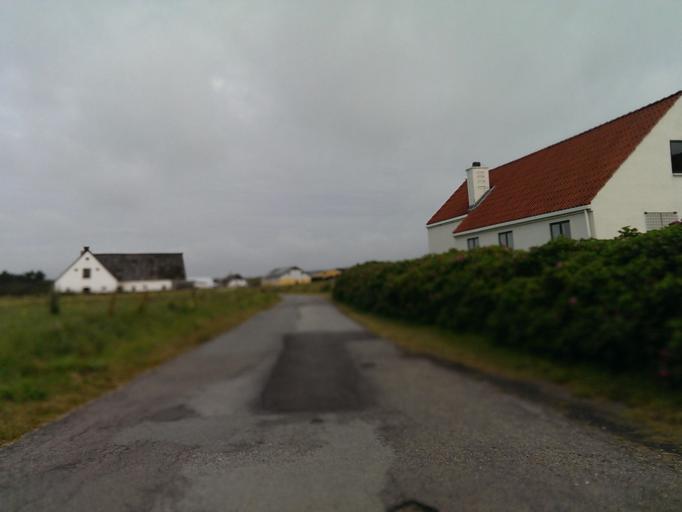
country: DK
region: North Denmark
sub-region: Jammerbugt Kommune
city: Pandrup
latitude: 57.3806
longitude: 9.7287
